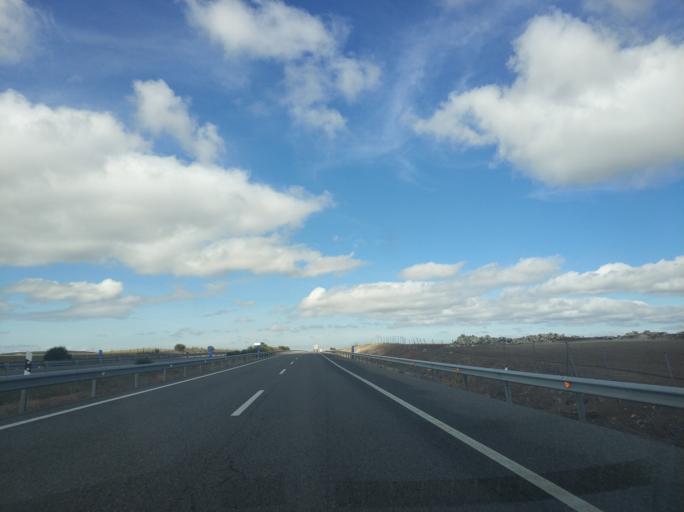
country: ES
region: Castille and Leon
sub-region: Provincia de Burgos
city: Albillos
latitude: 42.3045
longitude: -3.7727
